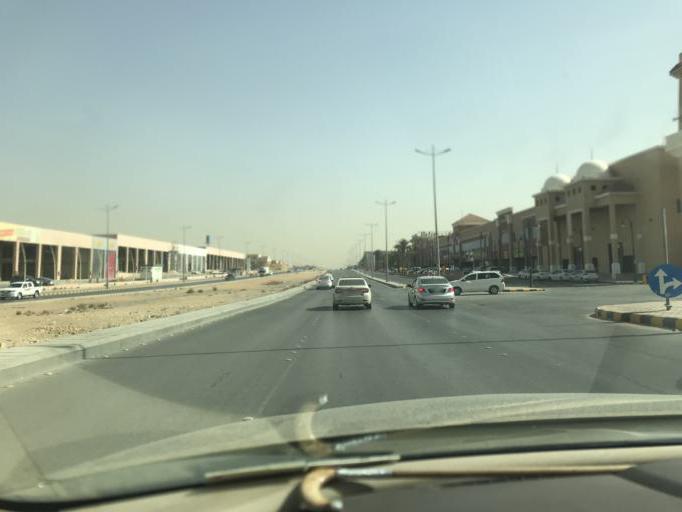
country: SA
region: Ar Riyad
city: Riyadh
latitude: 24.8127
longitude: 46.7338
